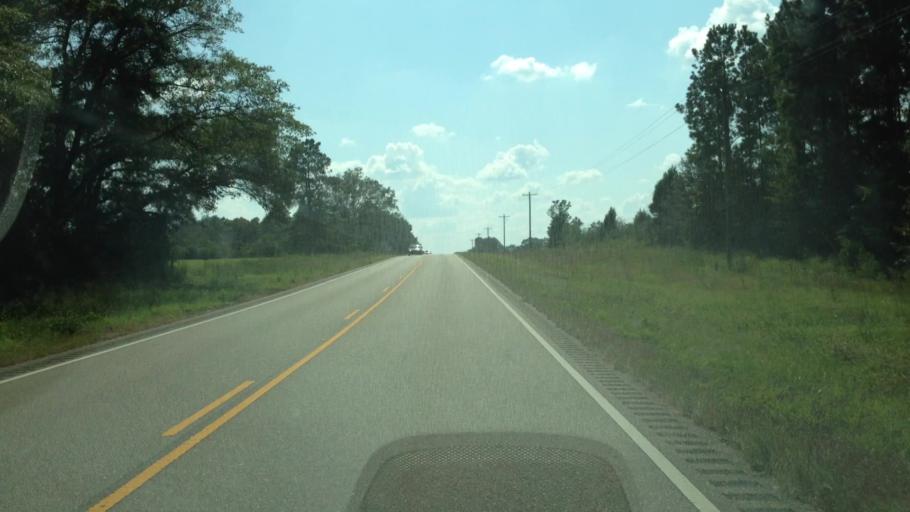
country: US
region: Alabama
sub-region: Covington County
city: Florala
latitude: 31.0443
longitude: -86.5924
